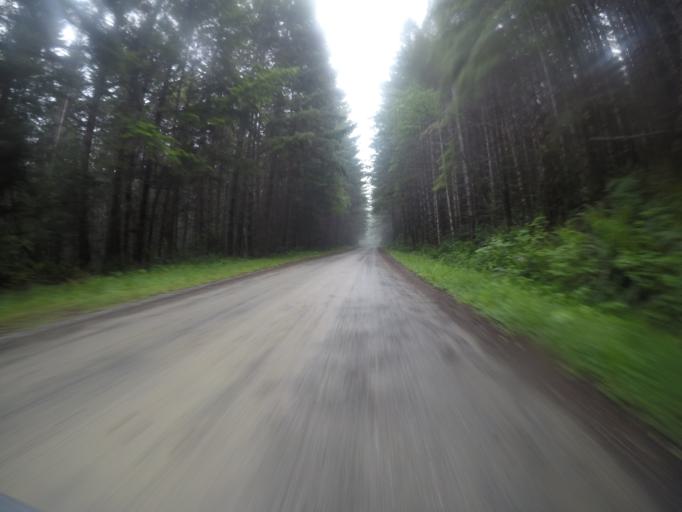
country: US
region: California
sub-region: Humboldt County
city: Westhaven-Moonstone
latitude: 41.2292
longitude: -123.9933
